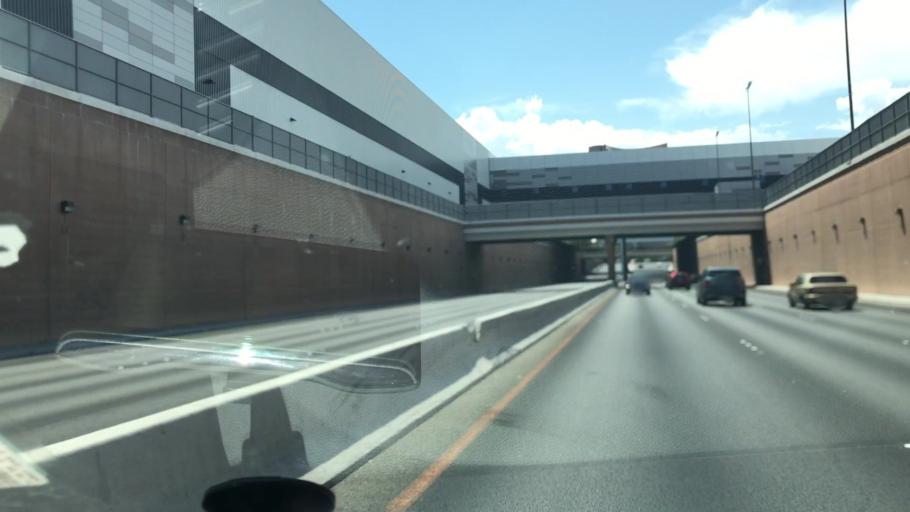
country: US
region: Nevada
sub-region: Clark County
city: Winchester
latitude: 36.1294
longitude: -115.1493
